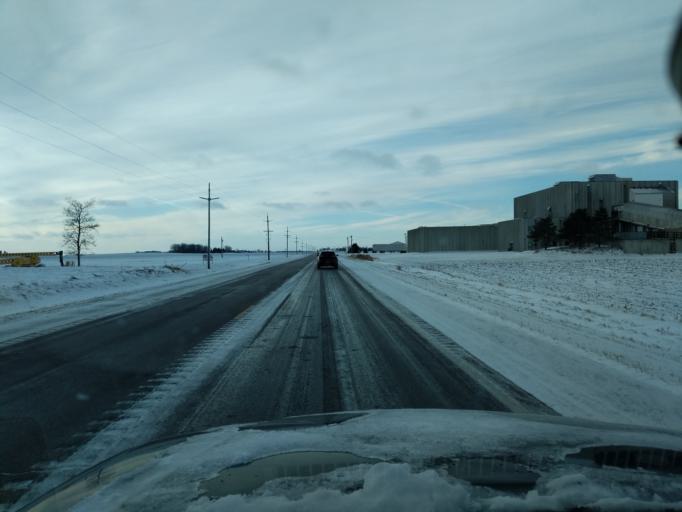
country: US
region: Minnesota
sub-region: Renville County
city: Hector
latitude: 44.7314
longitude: -94.5962
